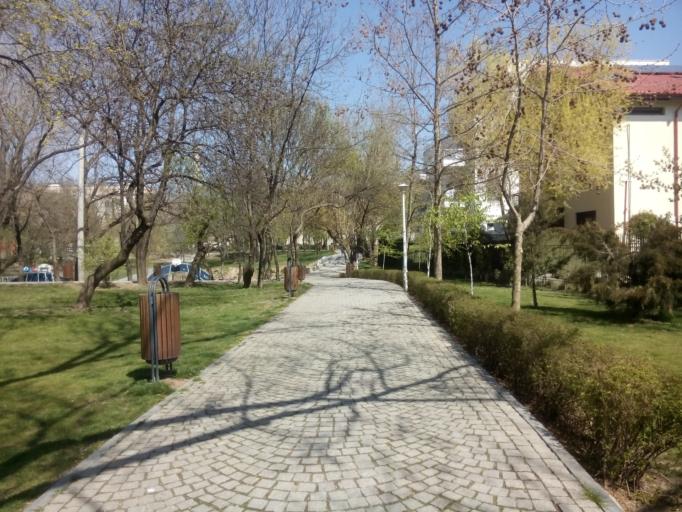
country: RO
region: Ilfov
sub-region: Comuna Fundeni-Dobroesti
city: Fundeni
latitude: 44.4311
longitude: 26.1508
